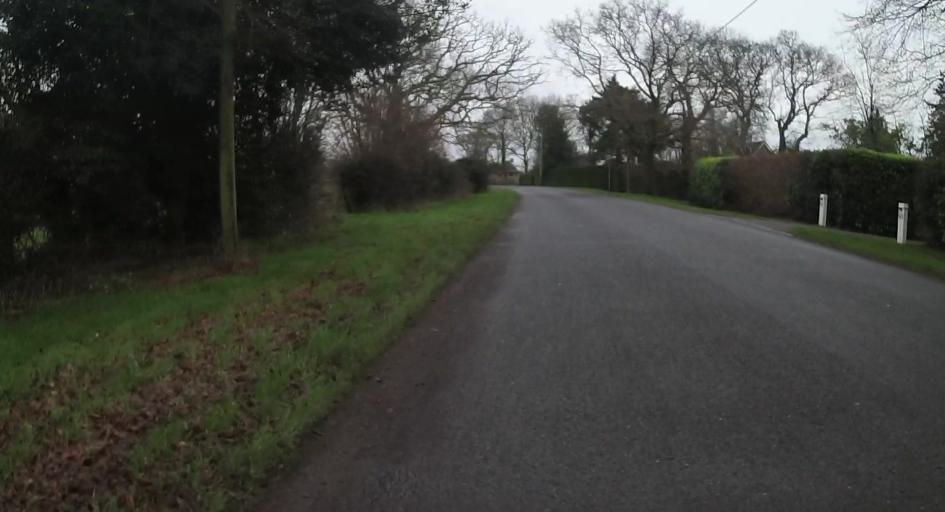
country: GB
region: England
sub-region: Hampshire
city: Four Marks
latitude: 51.1072
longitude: -1.0287
